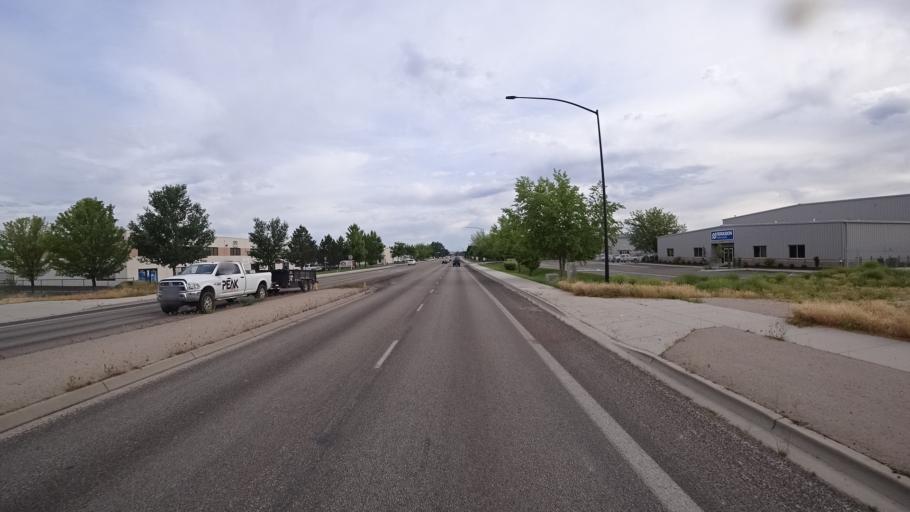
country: US
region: Idaho
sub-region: Ada County
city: Meridian
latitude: 43.6086
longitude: -116.3745
